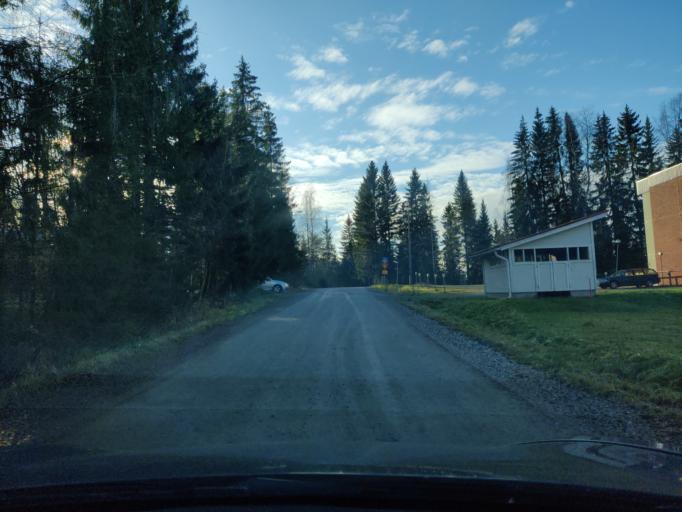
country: FI
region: Northern Savo
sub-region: Ylae-Savo
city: Kiuruvesi
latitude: 63.6450
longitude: 26.6341
